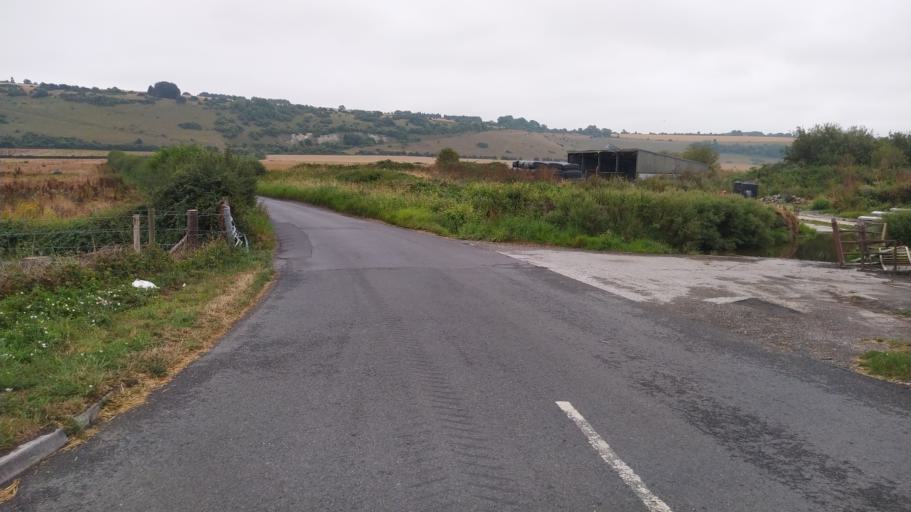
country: GB
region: England
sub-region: Wiltshire
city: Dinton
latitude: 51.0526
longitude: -1.9985
